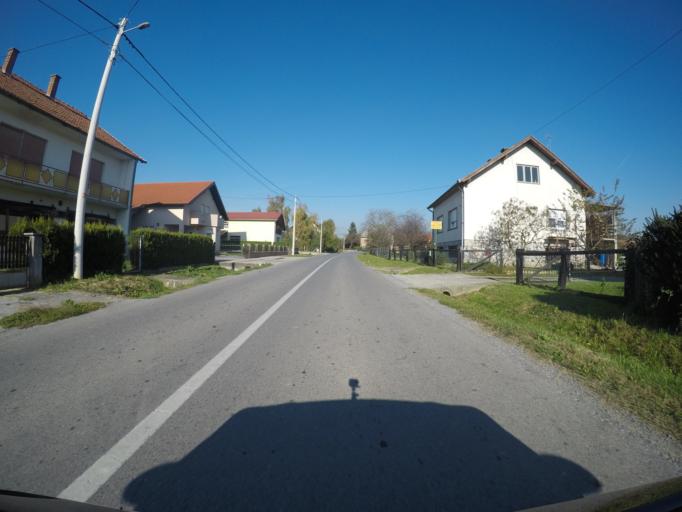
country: HR
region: Bjelovarsko-Bilogorska
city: Predavac
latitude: 45.9208
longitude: 16.7890
